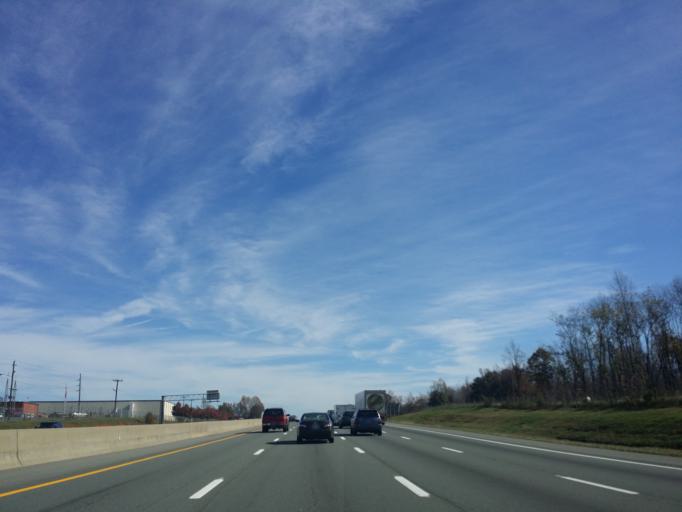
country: US
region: North Carolina
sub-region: Alamance County
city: Mebane
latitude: 36.0769
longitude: -79.2531
